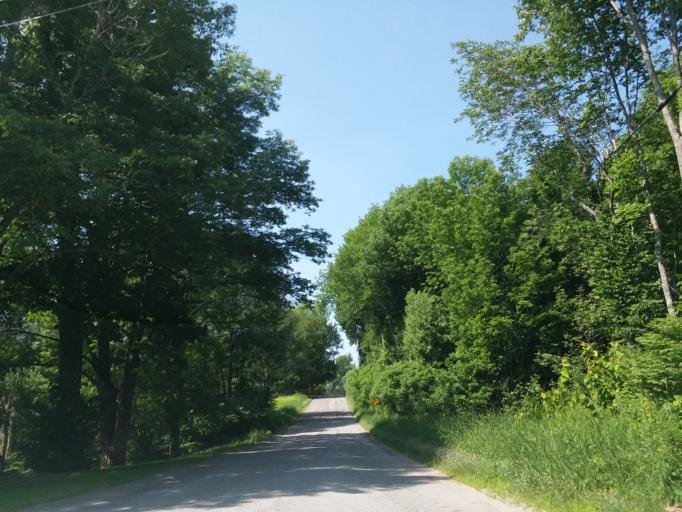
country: US
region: Maine
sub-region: Kennebec County
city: Winthrop
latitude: 44.2799
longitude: -70.0107
